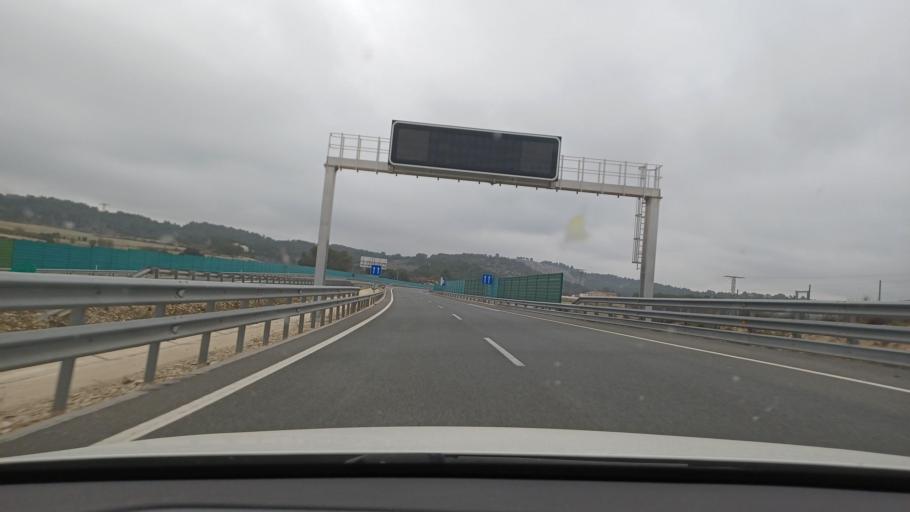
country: ES
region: Valencia
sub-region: Provincia de Alicante
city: Alcoy
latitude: 38.6509
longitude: -0.4740
